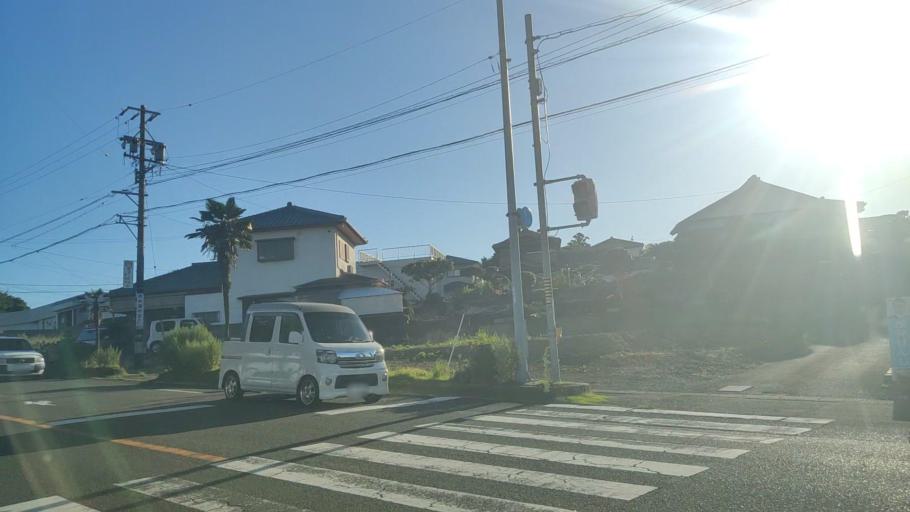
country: JP
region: Mie
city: Toba
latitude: 34.2855
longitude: 136.8829
